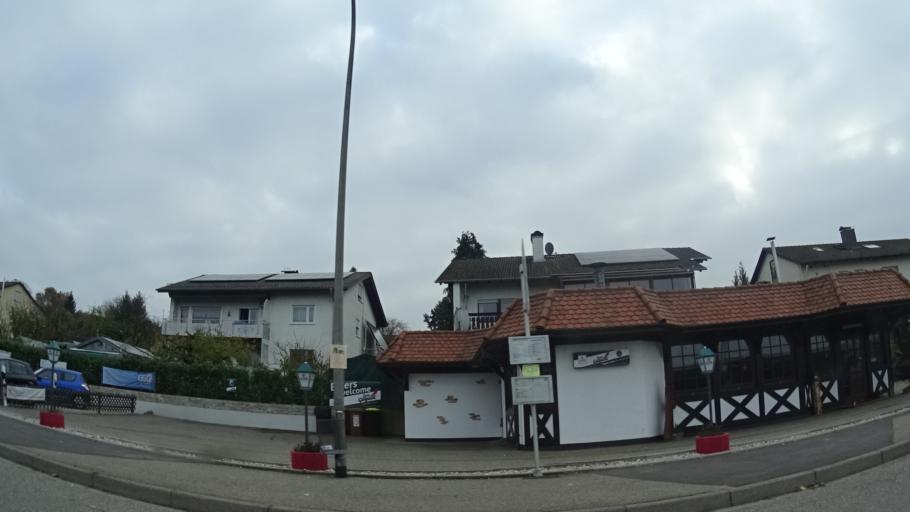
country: DE
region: Baden-Wuerttemberg
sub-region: Karlsruhe Region
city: Sinzheim
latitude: 48.7670
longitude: 8.1707
